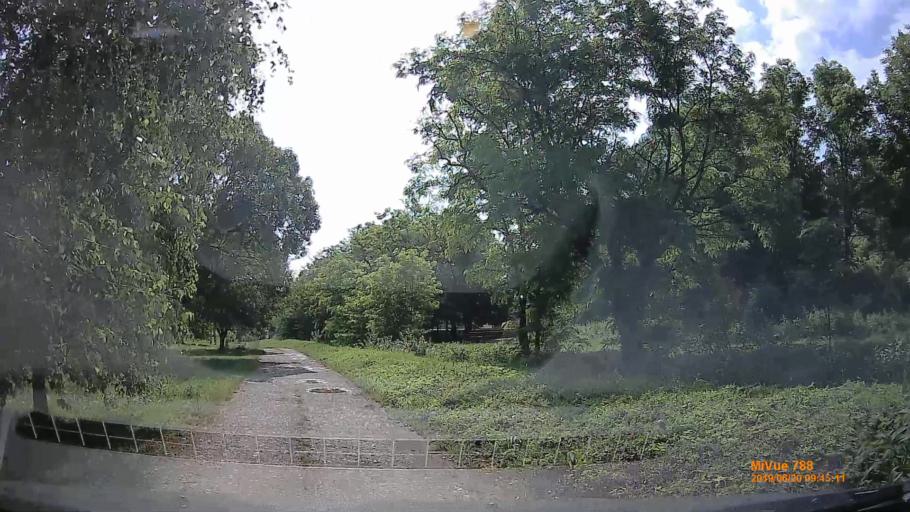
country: HU
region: Baranya
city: Pecsvarad
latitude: 46.1736
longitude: 18.4692
